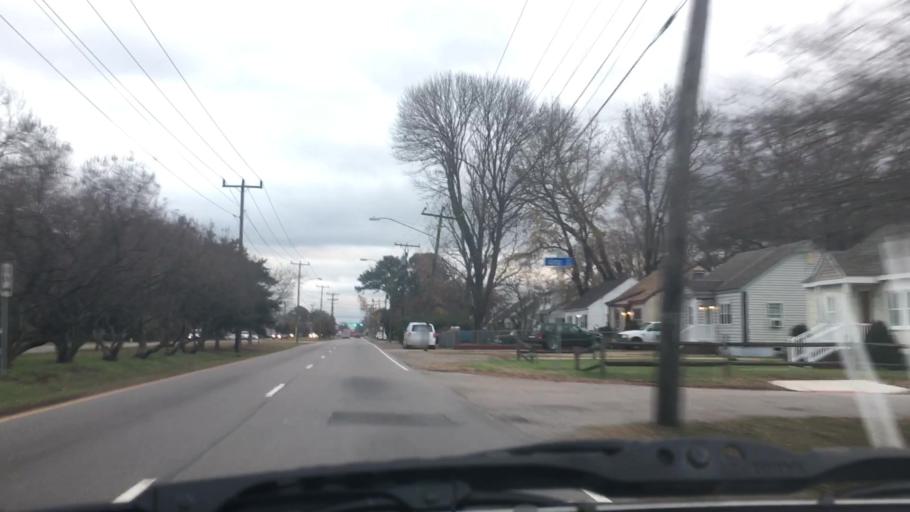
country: US
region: Virginia
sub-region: City of Norfolk
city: Norfolk
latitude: 36.9189
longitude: -76.2423
